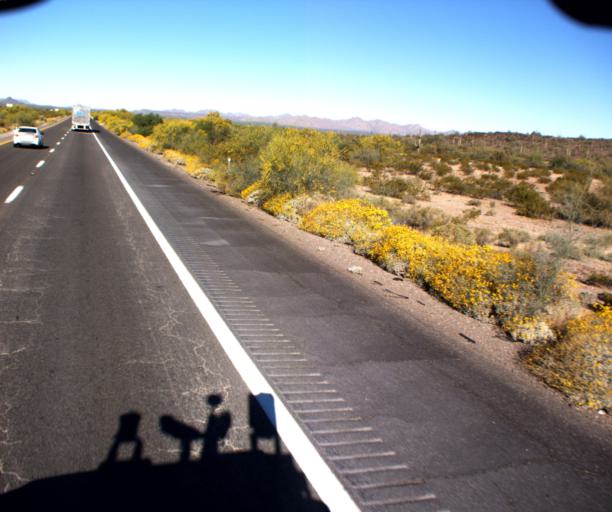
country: US
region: Arizona
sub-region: Pinal County
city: Maricopa
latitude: 32.8360
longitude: -112.1934
